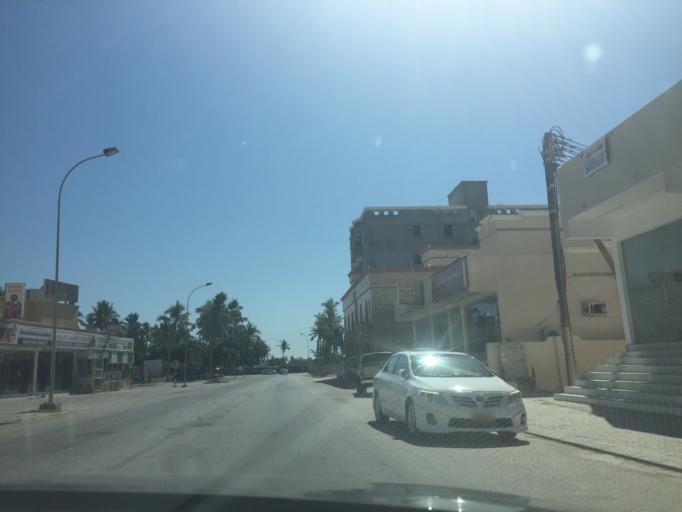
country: OM
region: Zufar
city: Salalah
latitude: 17.0198
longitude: 54.1573
